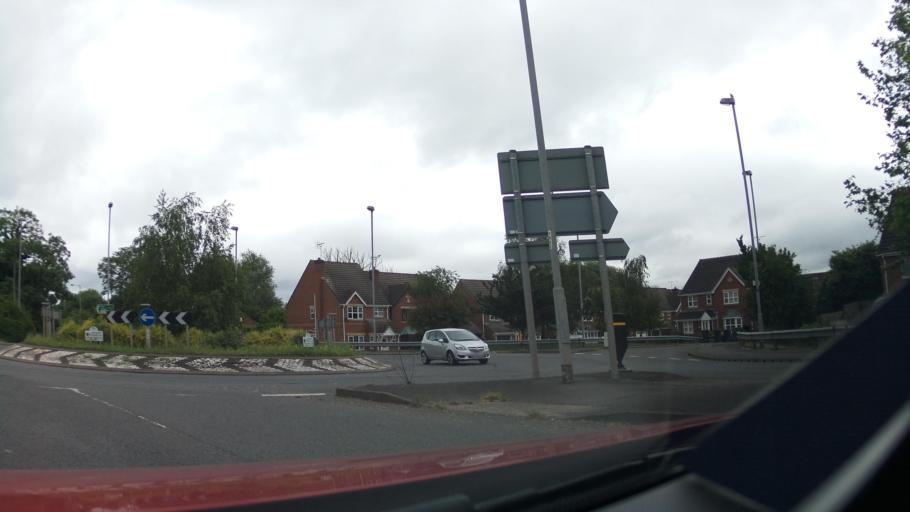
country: GB
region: England
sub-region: Staffordshire
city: Burton upon Trent
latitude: 52.8281
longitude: -1.6175
